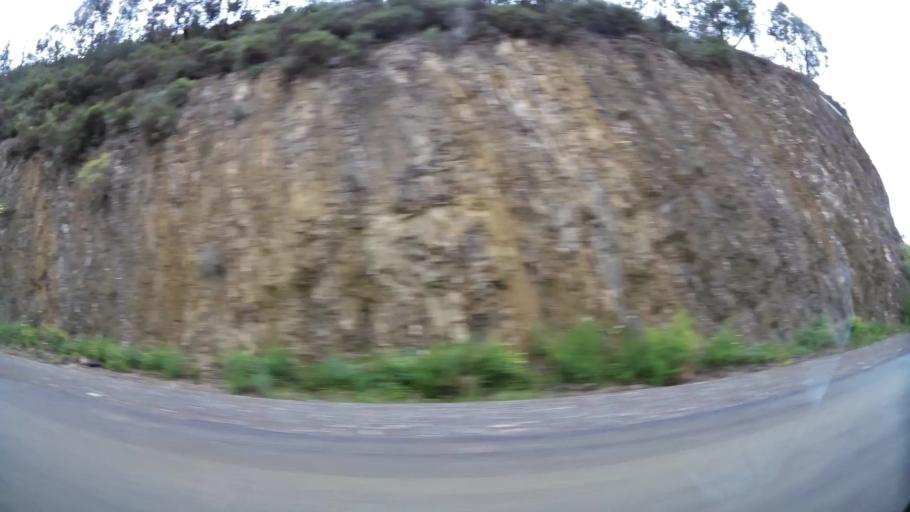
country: MA
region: Taza-Al Hoceima-Taounate
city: Imzourene
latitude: 34.9389
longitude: -3.8094
